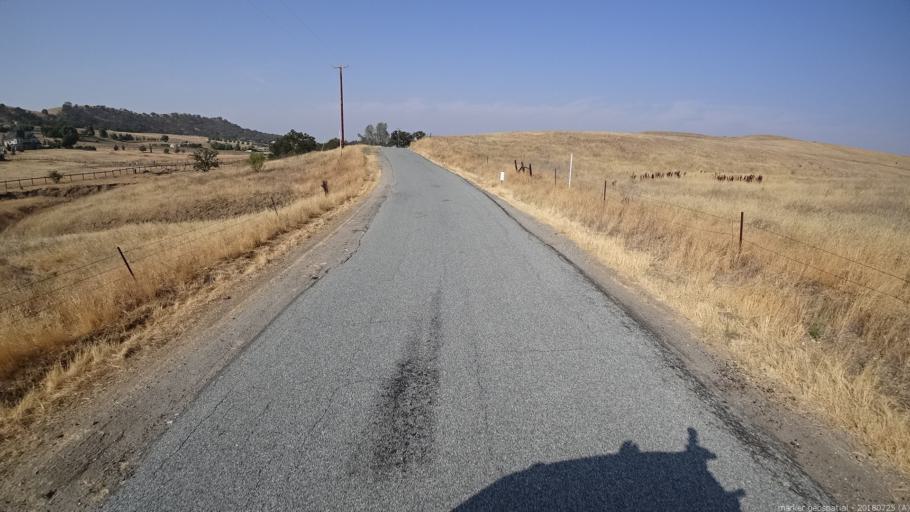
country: US
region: California
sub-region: San Luis Obispo County
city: San Miguel
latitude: 35.7983
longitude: -120.5701
